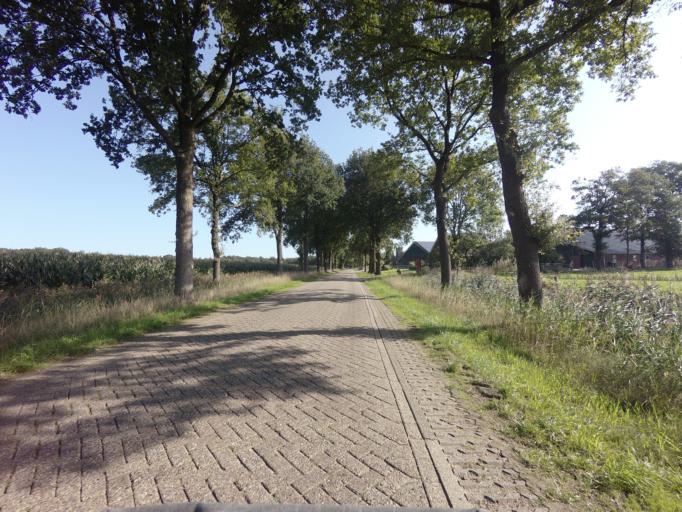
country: NL
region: Overijssel
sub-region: Gemeente Raalte
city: Raalte
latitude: 52.4229
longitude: 6.2938
